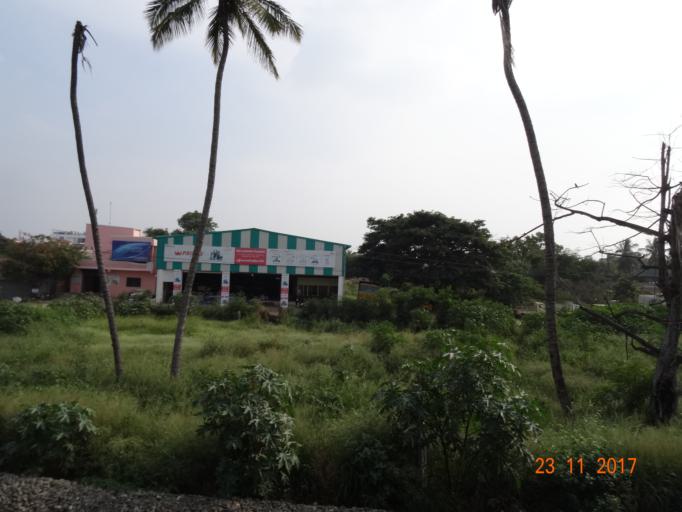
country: IN
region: Tamil Nadu
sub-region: Coimbatore
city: Coimbatore
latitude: 11.0276
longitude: 76.9742
